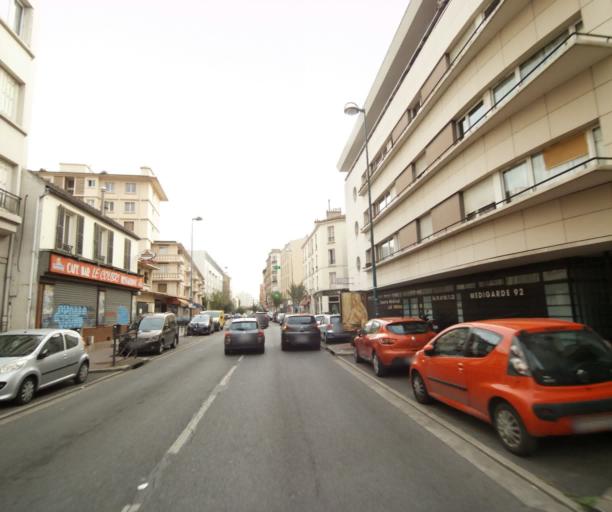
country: FR
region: Ile-de-France
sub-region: Departement des Hauts-de-Seine
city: Clichy
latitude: 48.9151
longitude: 2.3016
